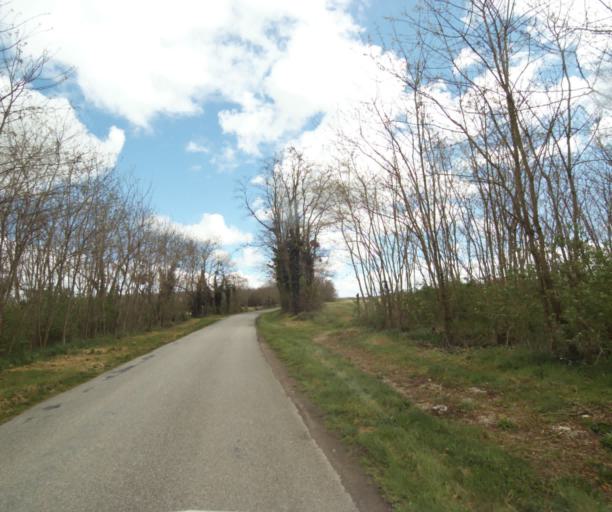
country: FR
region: Midi-Pyrenees
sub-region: Departement de l'Ariege
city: Saverdun
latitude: 43.2401
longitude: 1.6186
